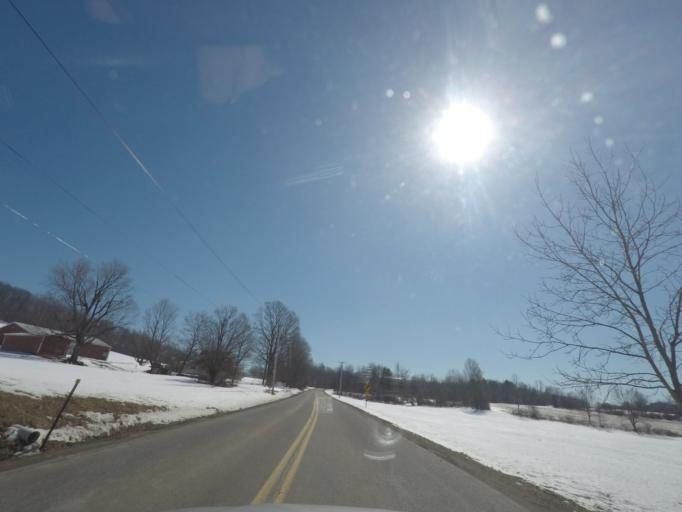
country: US
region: New York
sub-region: Saratoga County
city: Stillwater
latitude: 43.0311
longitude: -73.6721
